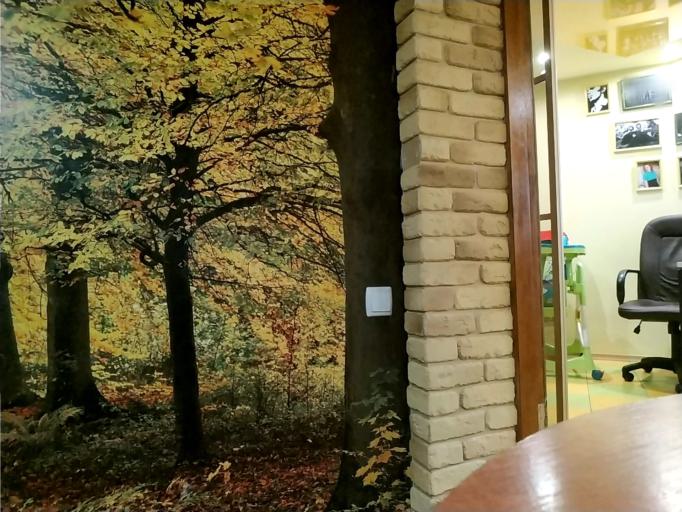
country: RU
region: Tverskaya
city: Staraya Toropa
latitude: 56.3398
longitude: 31.8552
